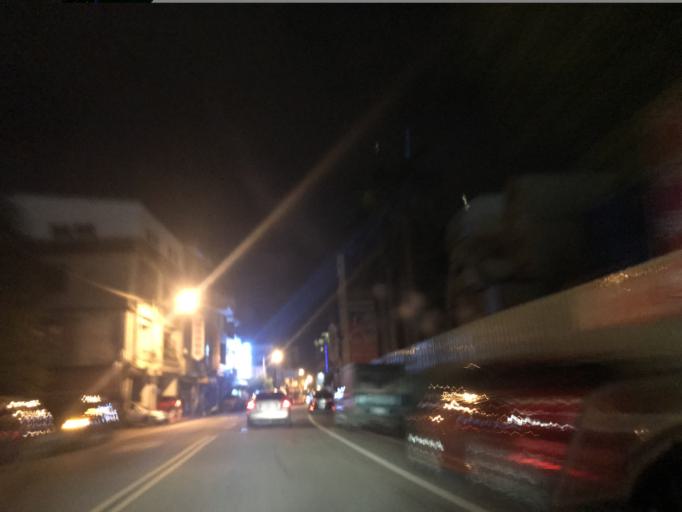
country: TW
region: Taiwan
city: Daxi
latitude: 24.8642
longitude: 121.2144
